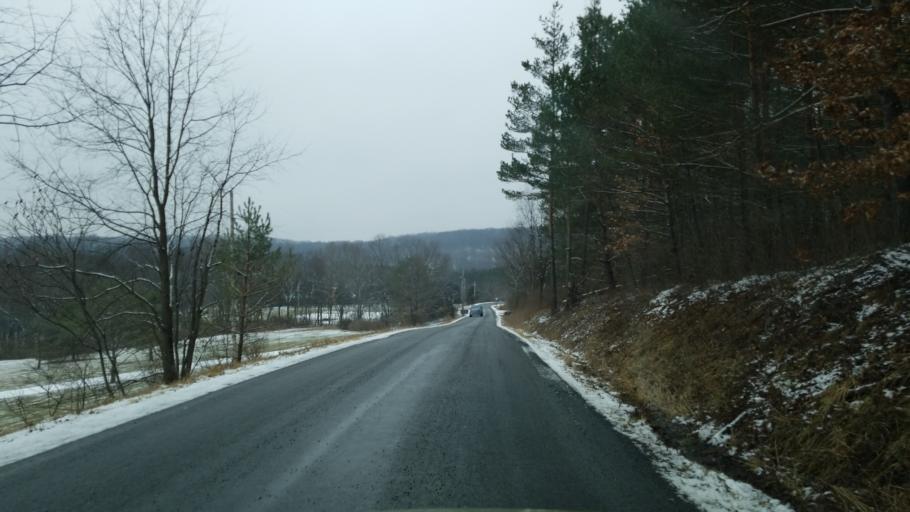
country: US
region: Pennsylvania
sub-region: Jefferson County
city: Sykesville
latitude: 41.0489
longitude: -78.7896
